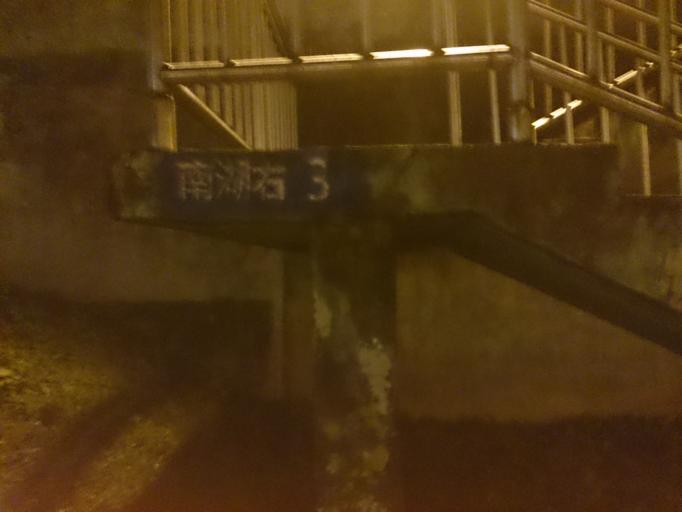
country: TW
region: Taipei
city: Taipei
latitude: 25.0626
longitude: 121.6104
